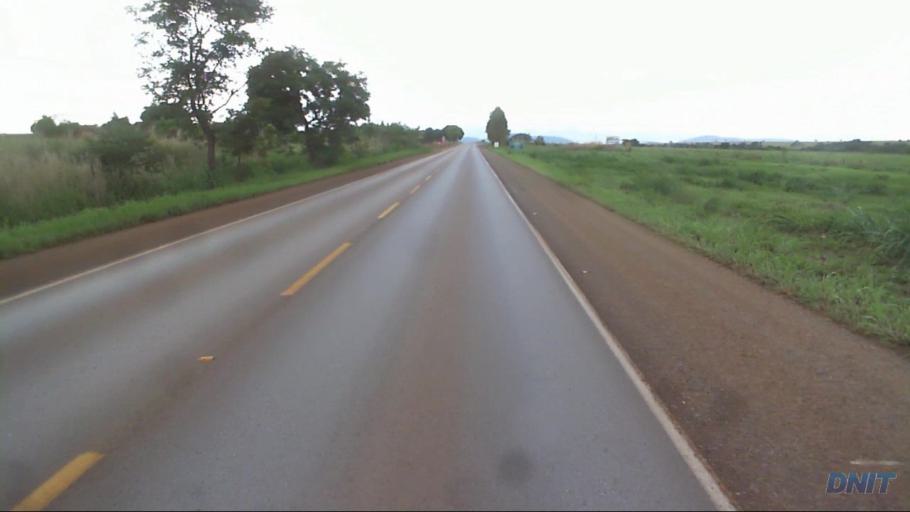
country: BR
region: Goias
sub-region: Barro Alto
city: Barro Alto
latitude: -14.8327
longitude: -49.0337
